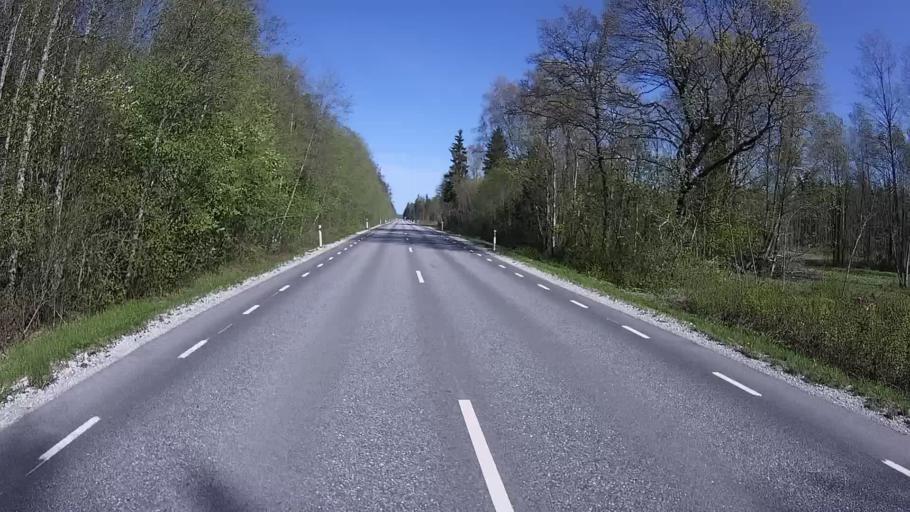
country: EE
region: Raplamaa
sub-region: Jaervakandi vald
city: Jarvakandi
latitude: 58.8529
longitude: 24.7933
